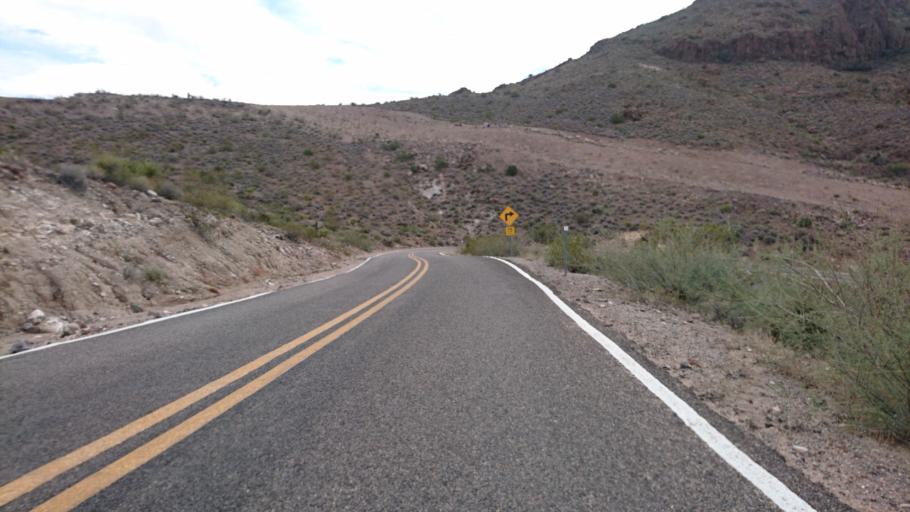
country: US
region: Arizona
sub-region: Mohave County
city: Golden Valley
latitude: 35.0466
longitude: -114.3627
